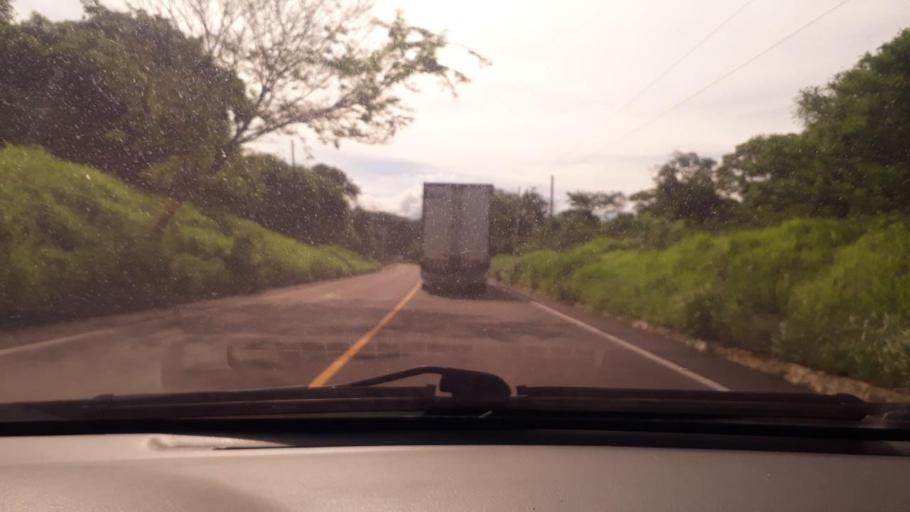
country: SV
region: Ahuachapan
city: San Francisco Menendez
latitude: 13.8786
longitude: -90.1222
